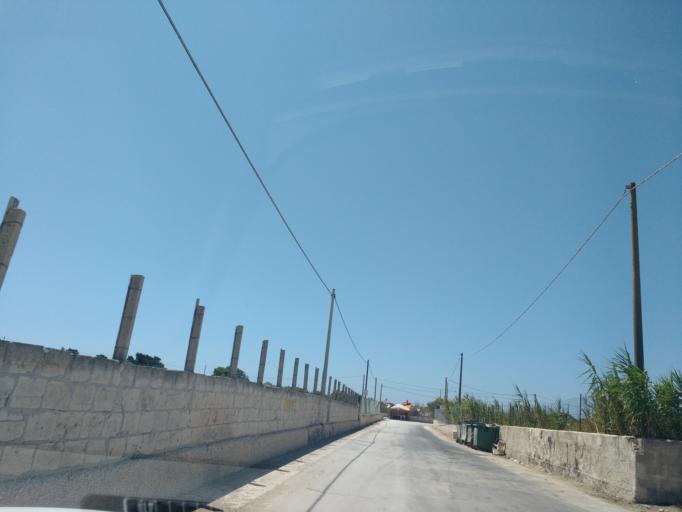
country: IT
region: Sicily
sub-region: Provincia di Siracusa
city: Portopalo di Capo Passero
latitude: 36.6601
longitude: 15.0805
